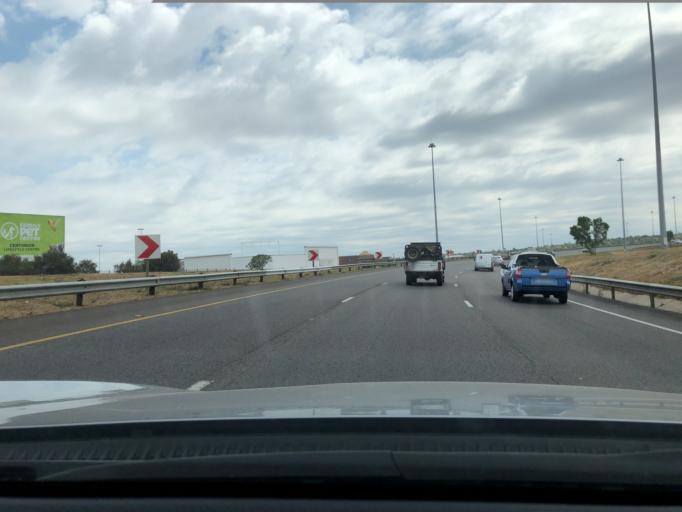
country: ZA
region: Gauteng
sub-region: City of Tshwane Metropolitan Municipality
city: Centurion
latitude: -25.8784
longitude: 28.1664
